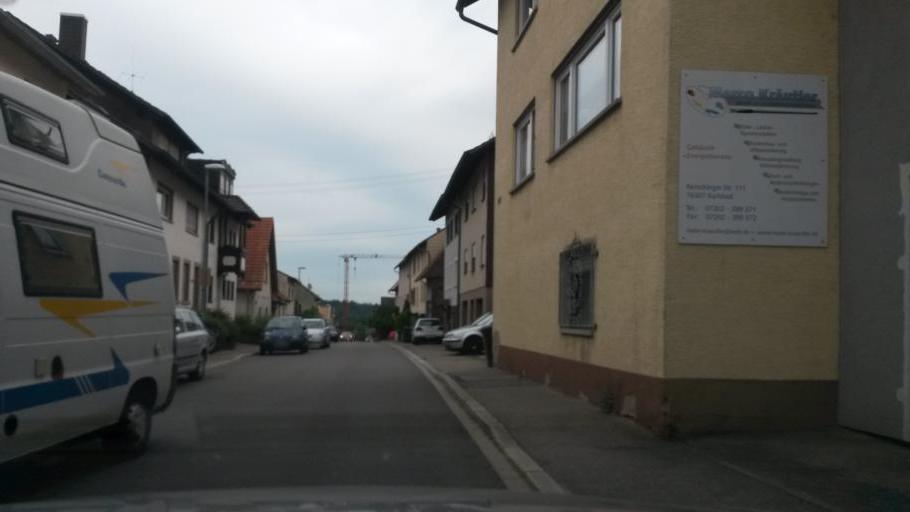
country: DE
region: Baden-Wuerttemberg
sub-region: Karlsruhe Region
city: Neuenburg
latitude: 48.9112
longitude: 8.5288
